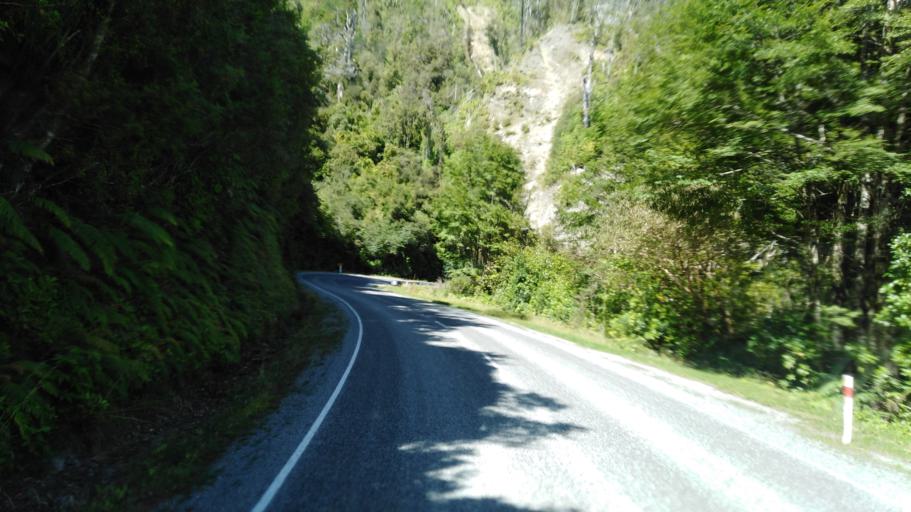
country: NZ
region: West Coast
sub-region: Buller District
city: Westport
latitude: -41.4947
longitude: 172.0480
